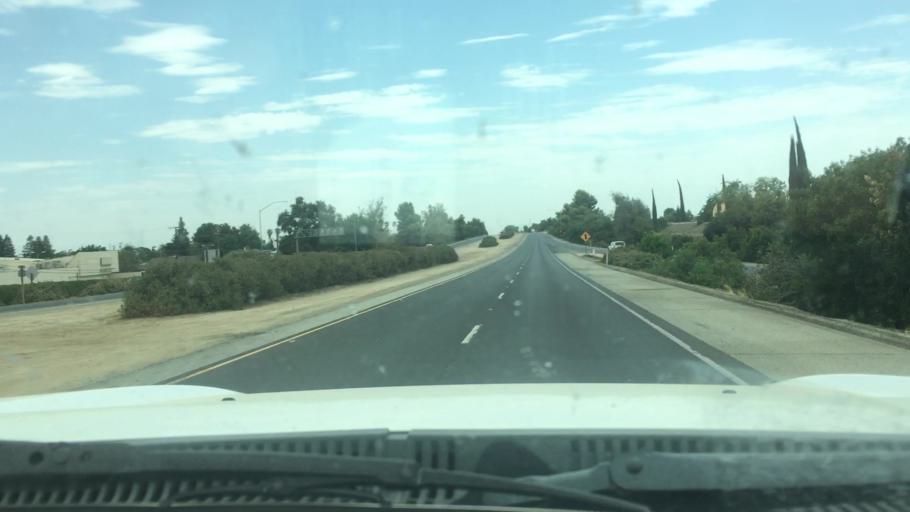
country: US
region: California
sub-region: Tulare County
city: Porterville
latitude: 36.0791
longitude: -119.0395
